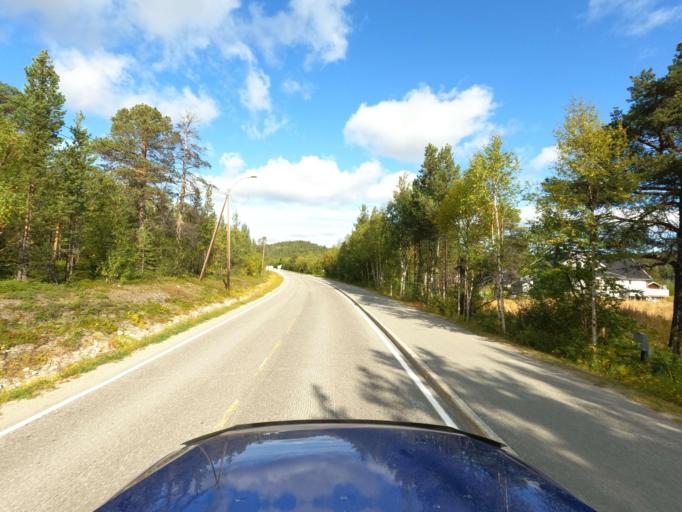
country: NO
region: Finnmark Fylke
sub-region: Karasjok
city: Karasjohka
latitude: 69.4771
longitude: 25.5167
